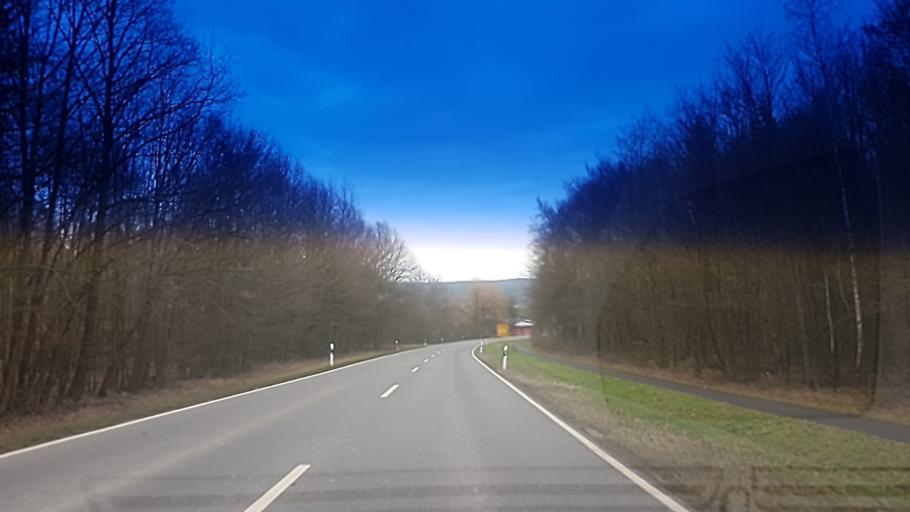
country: DE
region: Bavaria
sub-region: Upper Franconia
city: Memmelsdorf
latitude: 49.9071
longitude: 10.9743
